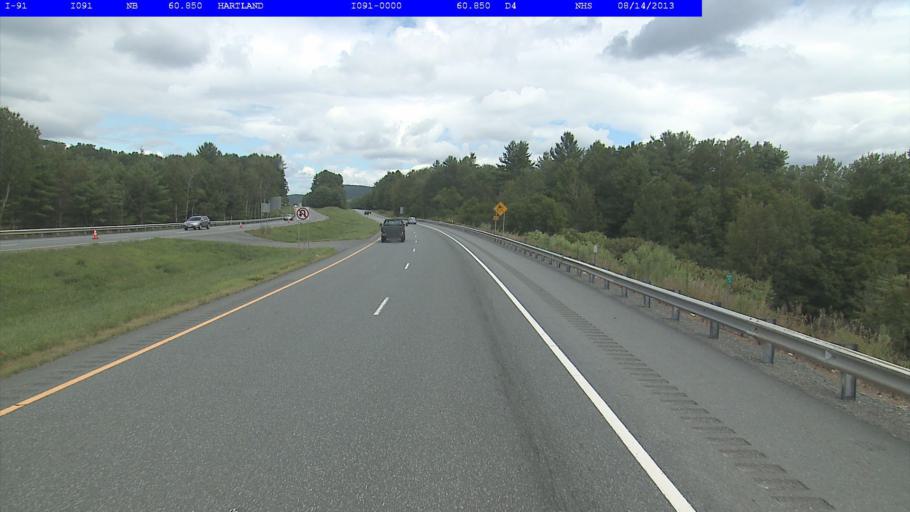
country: US
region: Vermont
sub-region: Windsor County
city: Windsor
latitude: 43.5311
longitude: -72.3961
